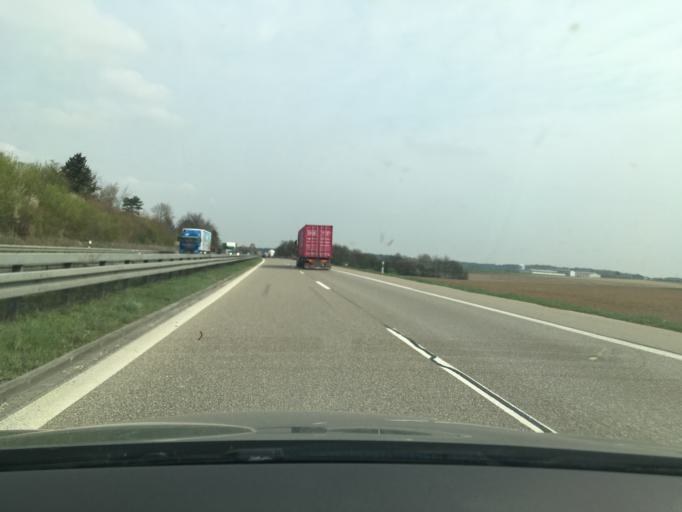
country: DE
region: Baden-Wuerttemberg
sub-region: Tuebingen Region
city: Huttisheim
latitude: 48.3309
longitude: 9.9428
